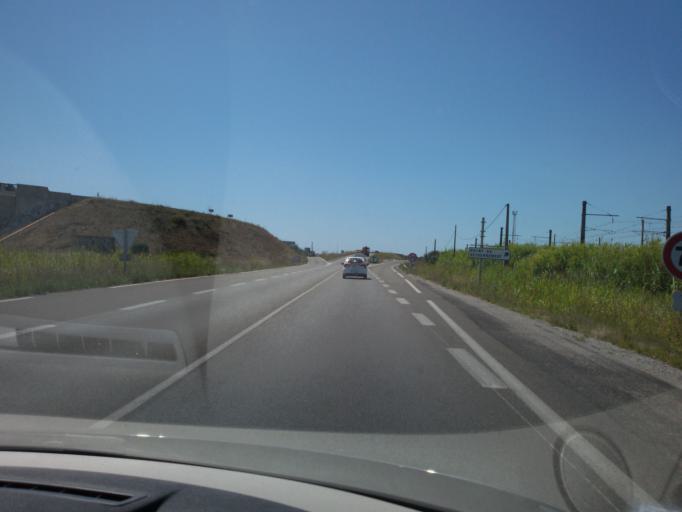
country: FR
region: Languedoc-Roussillon
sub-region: Departement de l'Herault
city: Frontignan
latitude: 43.4288
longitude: 3.7531
